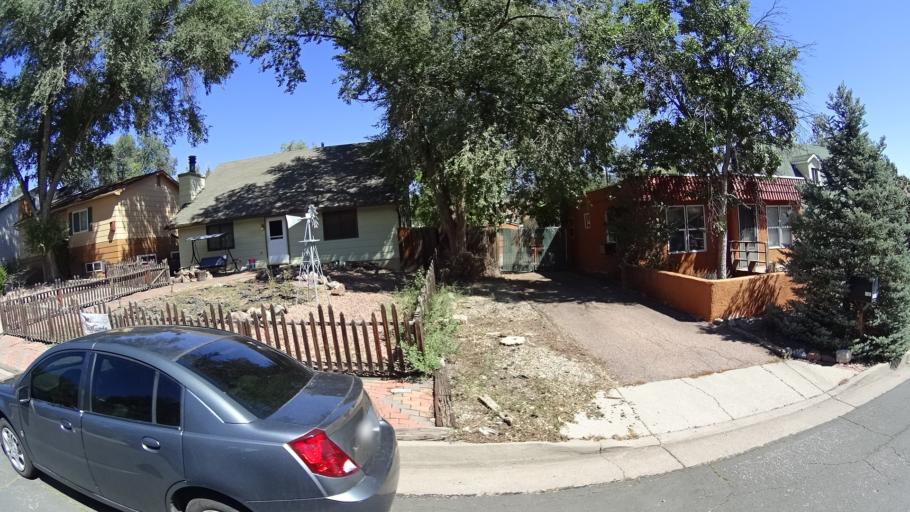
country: US
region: Colorado
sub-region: El Paso County
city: Colorado Springs
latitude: 38.8525
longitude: -104.8586
